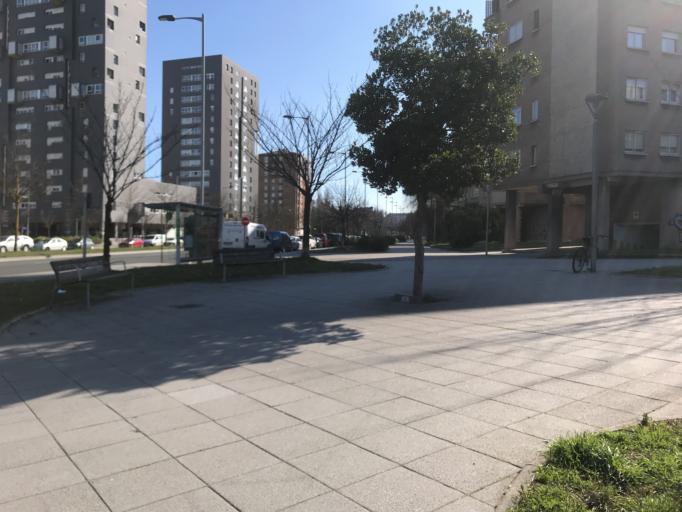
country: ES
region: Basque Country
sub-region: Provincia de Alava
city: Gasteiz / Vitoria
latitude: 42.8550
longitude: -2.6576
